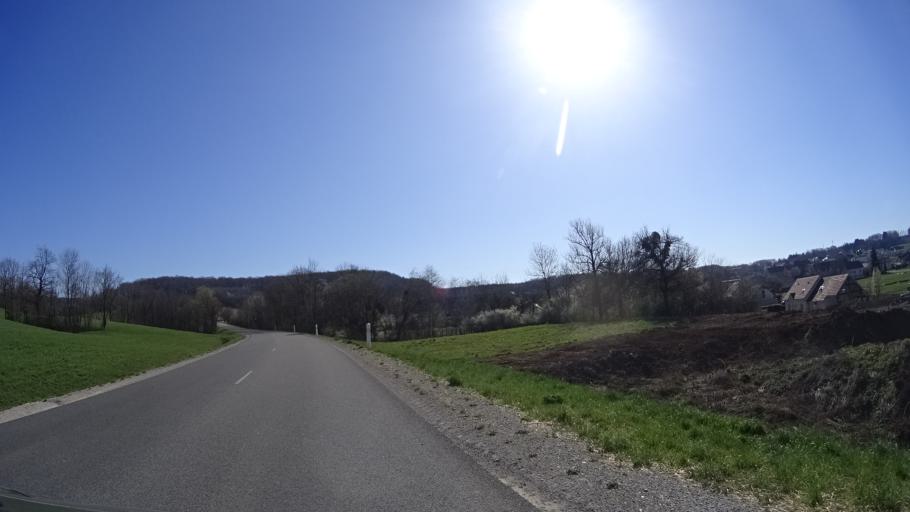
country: FR
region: Franche-Comte
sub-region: Departement du Doubs
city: Saone
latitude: 47.1601
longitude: 6.1063
